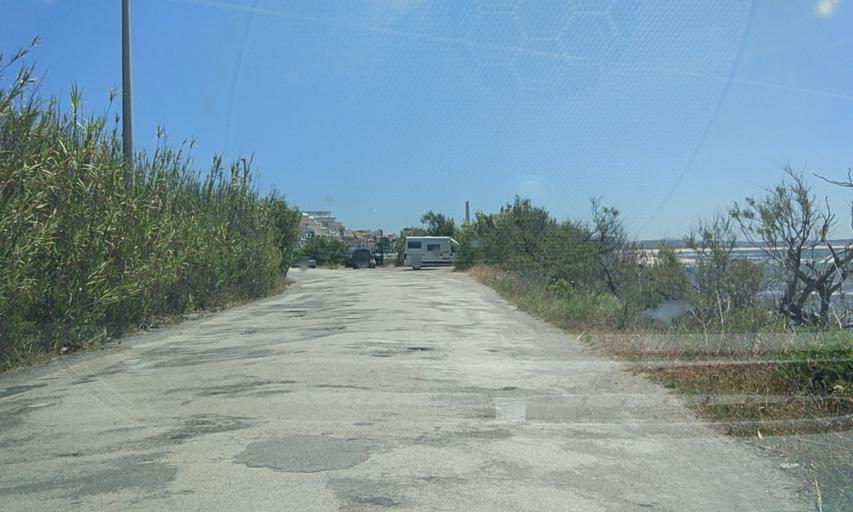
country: PT
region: Coimbra
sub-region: Figueira da Foz
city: Buarcos
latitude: 40.1776
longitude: -8.9015
